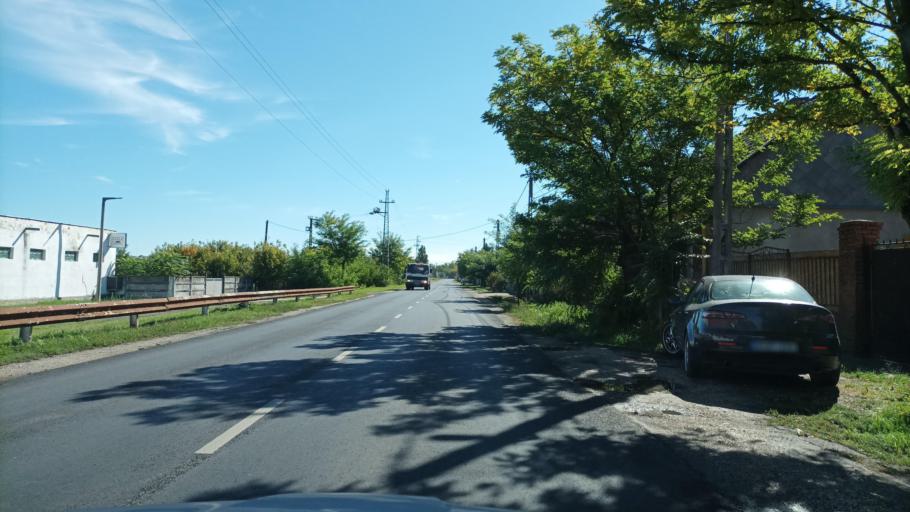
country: HU
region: Pest
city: Cegled
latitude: 47.1709
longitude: 19.8208
